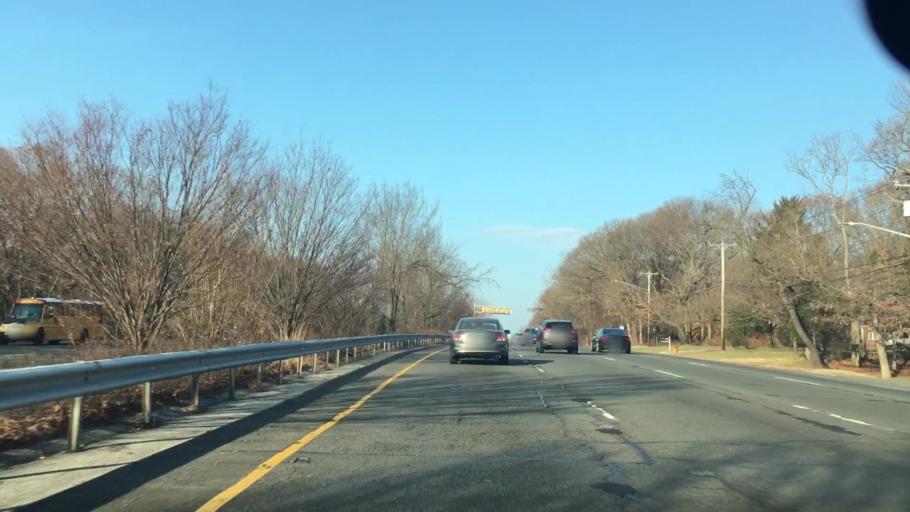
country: US
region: New York
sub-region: Suffolk County
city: Hauppauge
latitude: 40.8264
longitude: -73.2407
